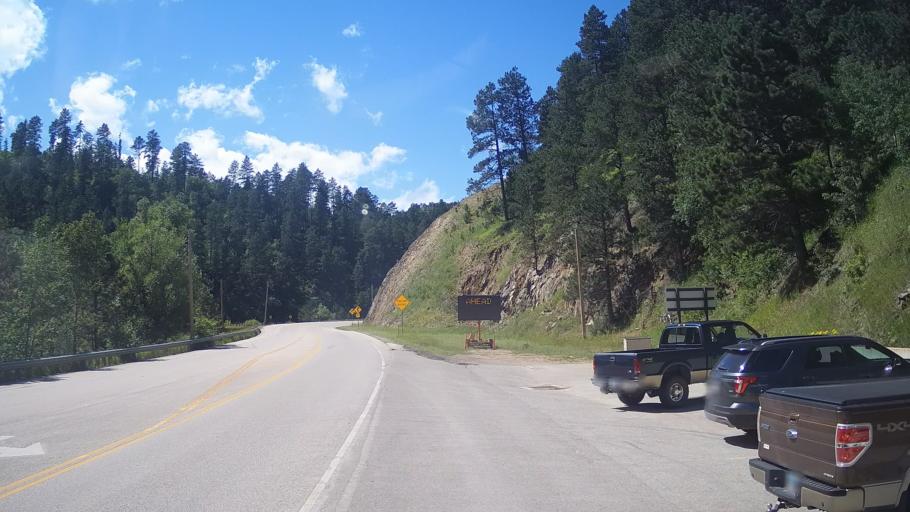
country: US
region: South Dakota
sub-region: Lawrence County
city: Deadwood
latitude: 44.3708
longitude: -103.7437
